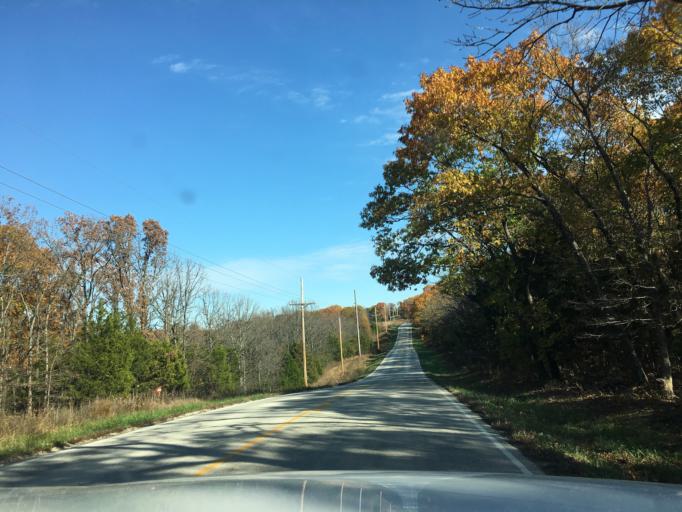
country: US
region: Missouri
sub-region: Maries County
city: Belle
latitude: 38.3366
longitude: -91.7697
